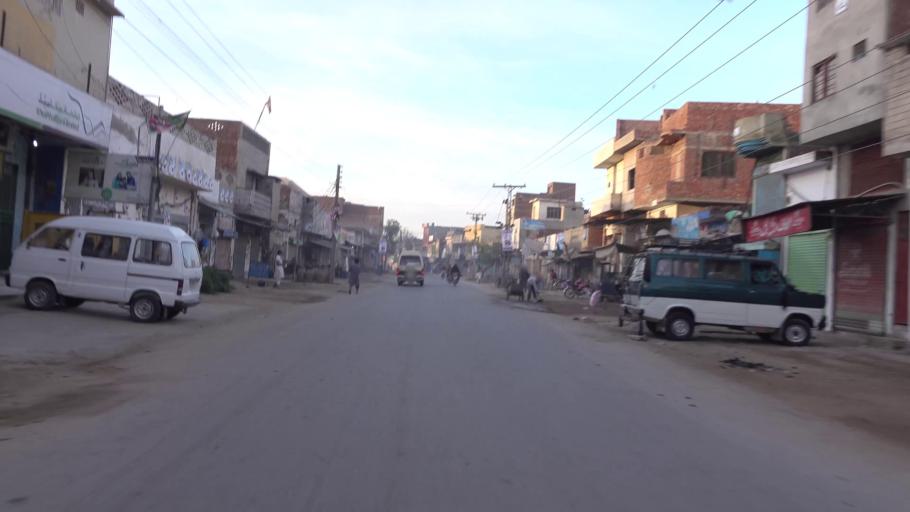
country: PK
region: Punjab
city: Hafizabad
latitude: 32.0680
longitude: 73.6889
